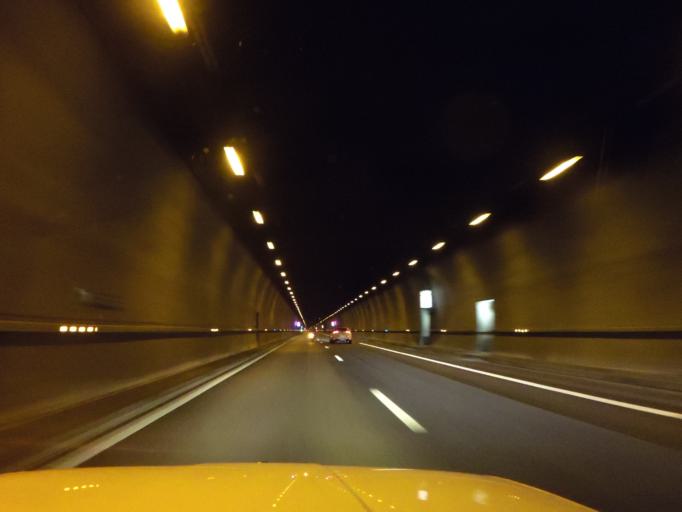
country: FR
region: Rhone-Alpes
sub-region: Departement de la Savoie
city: Novalaise
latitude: 45.5802
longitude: 5.8154
